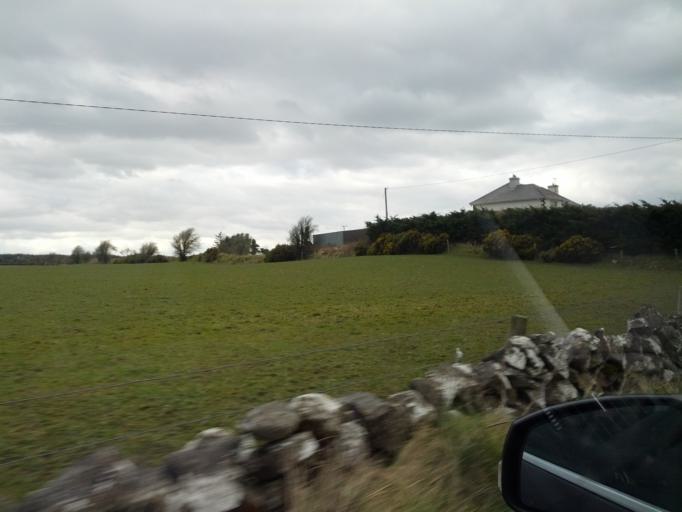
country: IE
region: Connaught
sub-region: County Galway
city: Athenry
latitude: 53.4112
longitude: -8.6347
